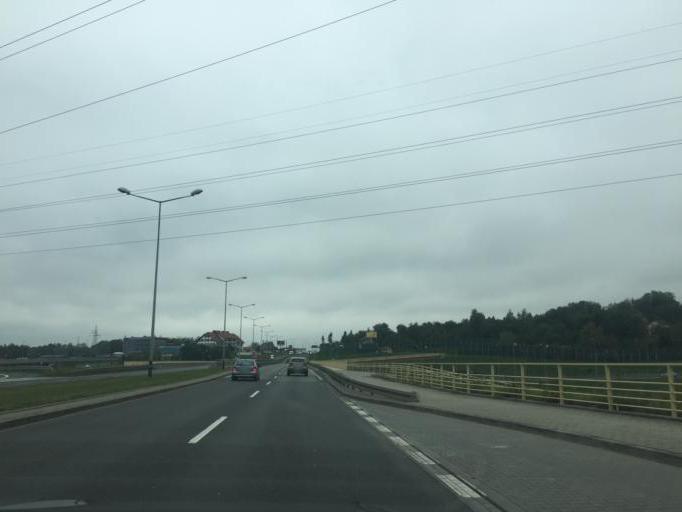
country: PL
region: Lesser Poland Voivodeship
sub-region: Powiat wielicki
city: Czarnochowice
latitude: 50.0059
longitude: 20.0182
